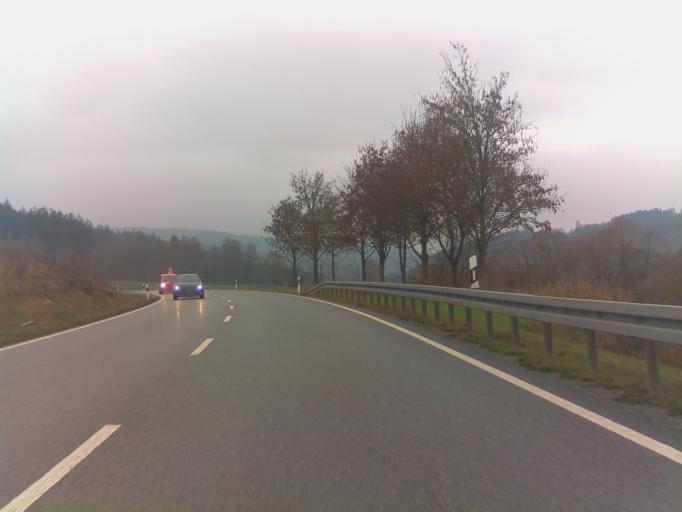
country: DE
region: Thuringia
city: Schleusingen
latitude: 50.4917
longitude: 10.7132
